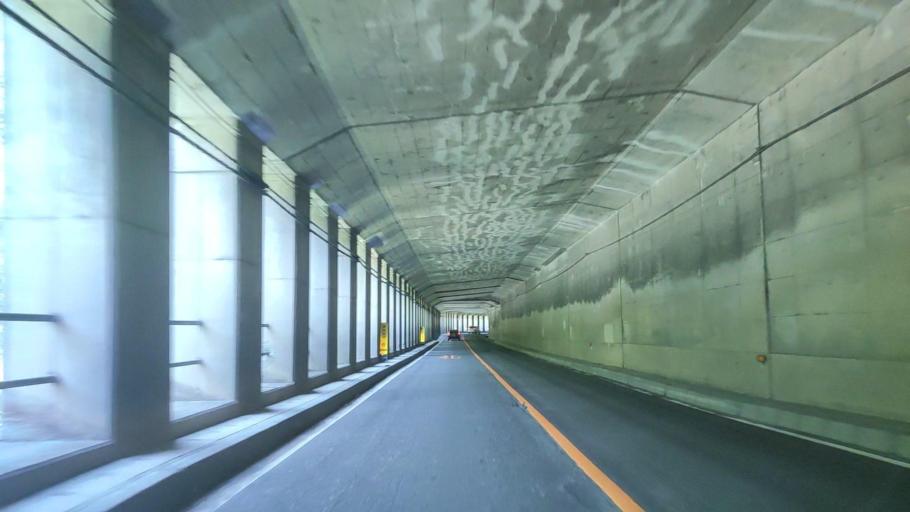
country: JP
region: Niigata
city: Itoigawa
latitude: 36.9053
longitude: 137.8655
